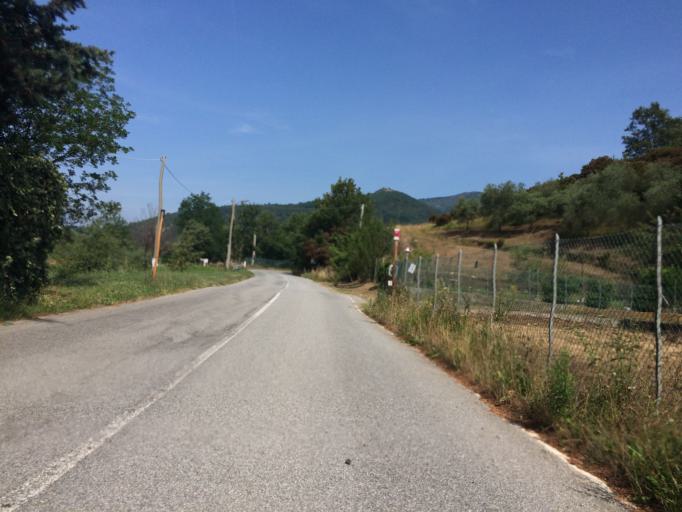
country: IT
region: Liguria
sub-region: Provincia di Savona
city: Varazze
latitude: 44.3851
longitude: 8.5686
